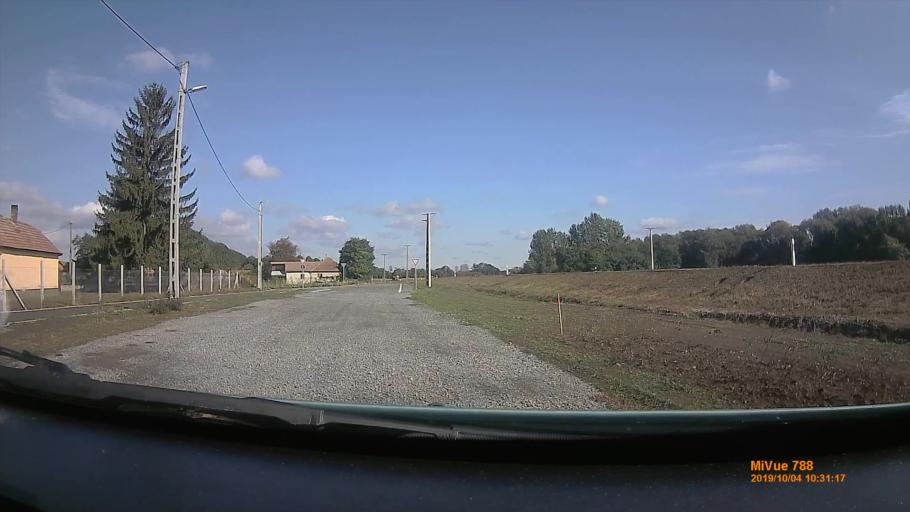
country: HU
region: Szabolcs-Szatmar-Bereg
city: Nyirtelek
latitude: 47.9613
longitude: 21.6566
